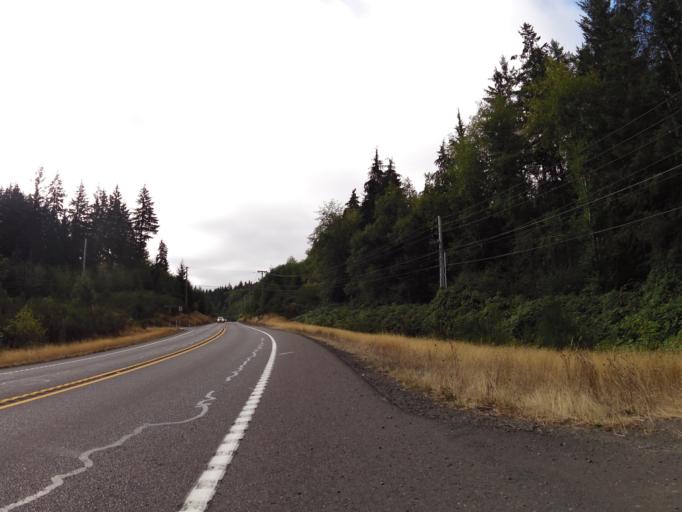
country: US
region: Washington
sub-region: Mason County
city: Allyn
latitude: 47.4059
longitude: -122.8397
